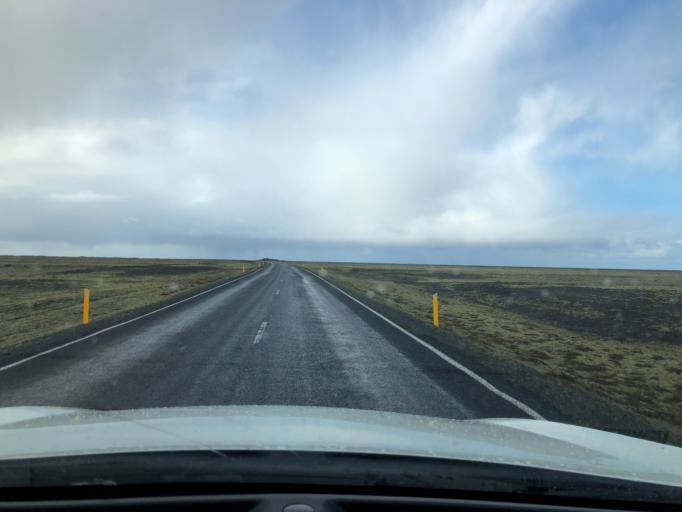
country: IS
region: South
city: Vestmannaeyjar
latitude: 63.6053
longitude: -18.4626
